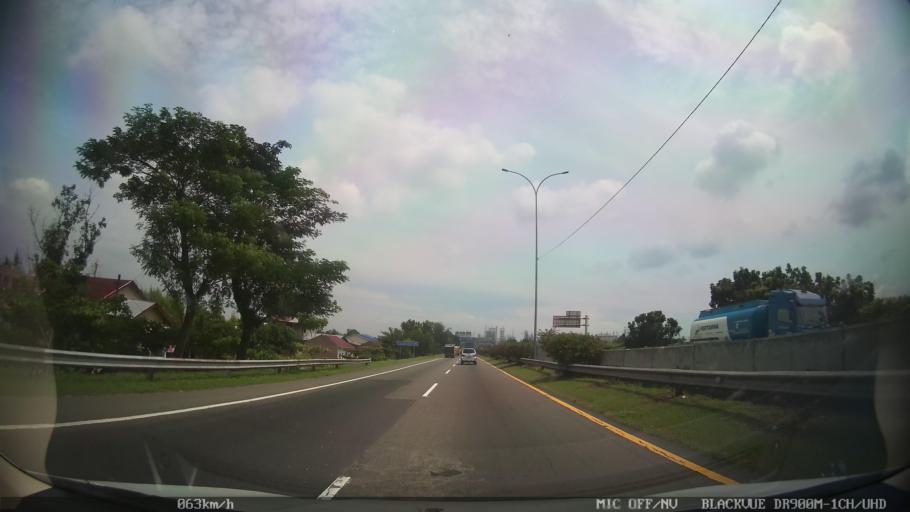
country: ID
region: North Sumatra
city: Medan
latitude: 3.6549
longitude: 98.6826
